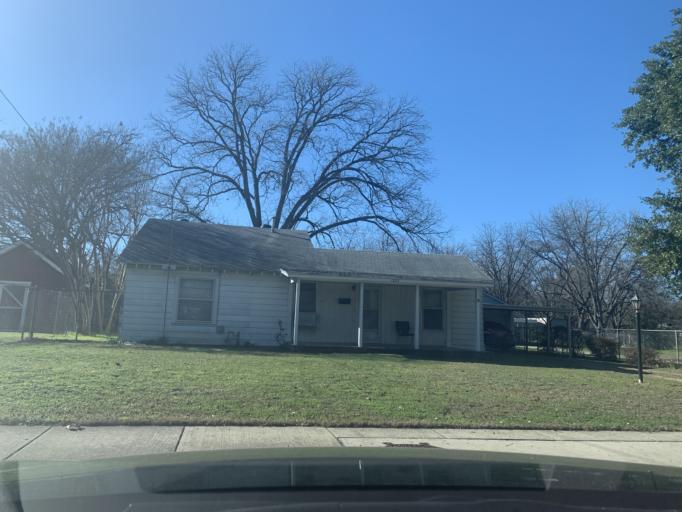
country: US
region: Texas
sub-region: Tarrant County
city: Haltom City
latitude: 32.7837
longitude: -97.2767
